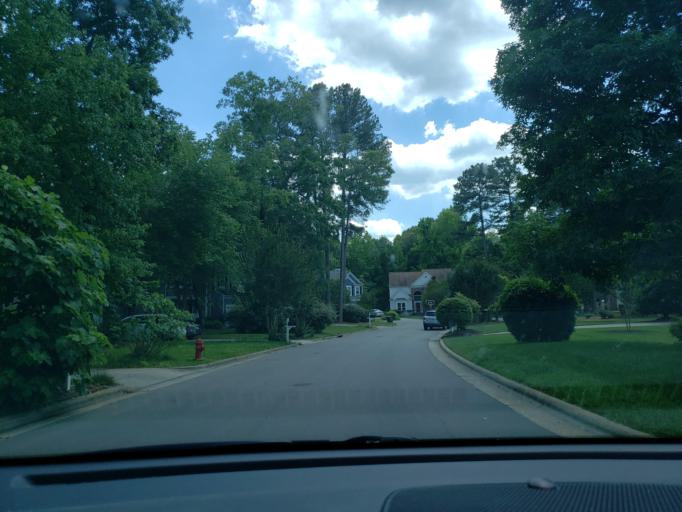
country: US
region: North Carolina
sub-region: Orange County
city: Chapel Hill
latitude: 35.9666
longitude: -78.9912
